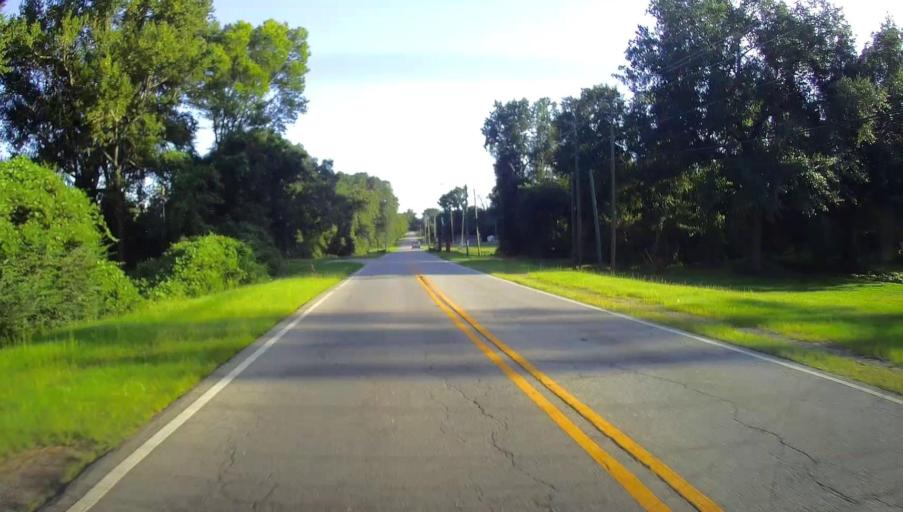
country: US
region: Georgia
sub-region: Muscogee County
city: Columbus
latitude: 32.4358
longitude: -85.0121
